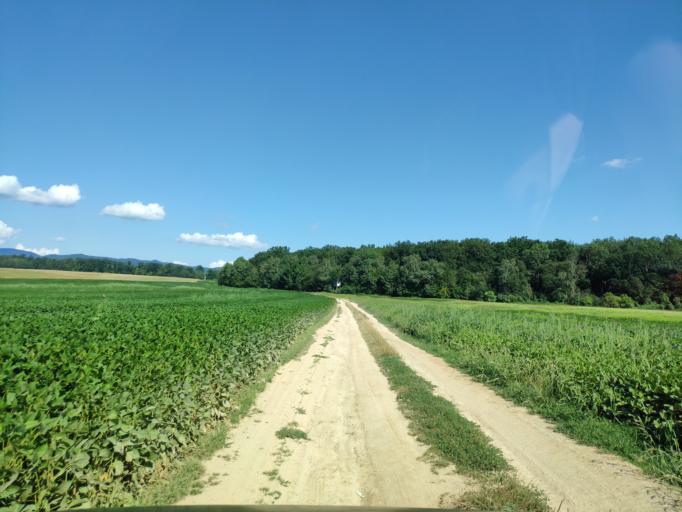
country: SK
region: Presovsky
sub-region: Okres Presov
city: Presov
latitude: 48.9064
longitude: 21.2845
